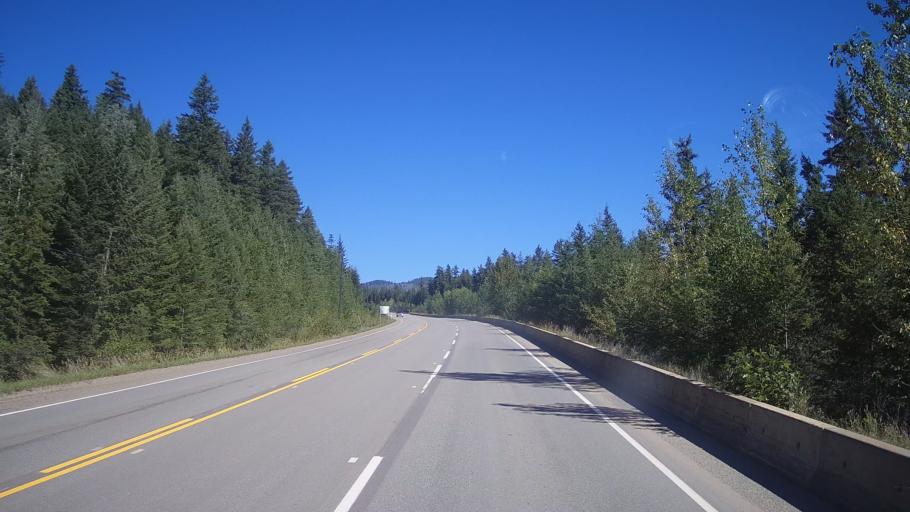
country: CA
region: British Columbia
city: Kamloops
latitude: 51.4610
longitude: -120.2303
